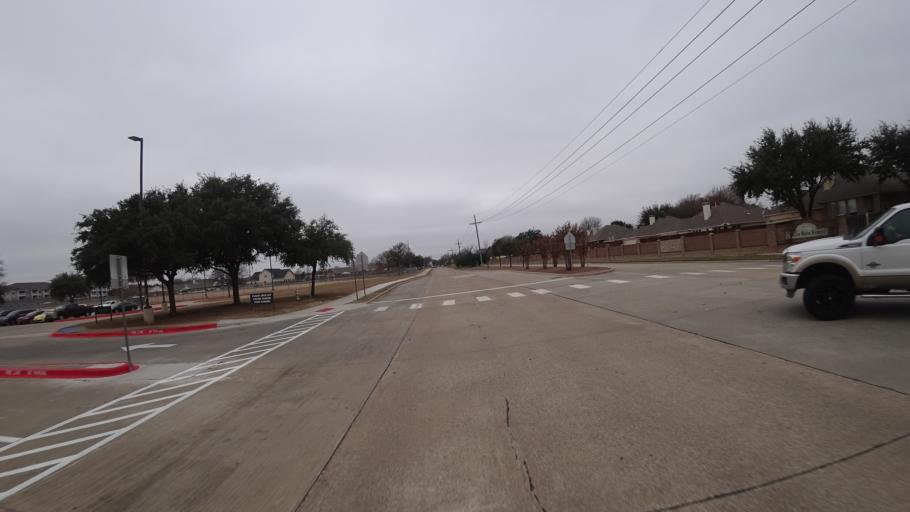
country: US
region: Texas
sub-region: Denton County
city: Highland Village
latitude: 33.0567
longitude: -97.0323
